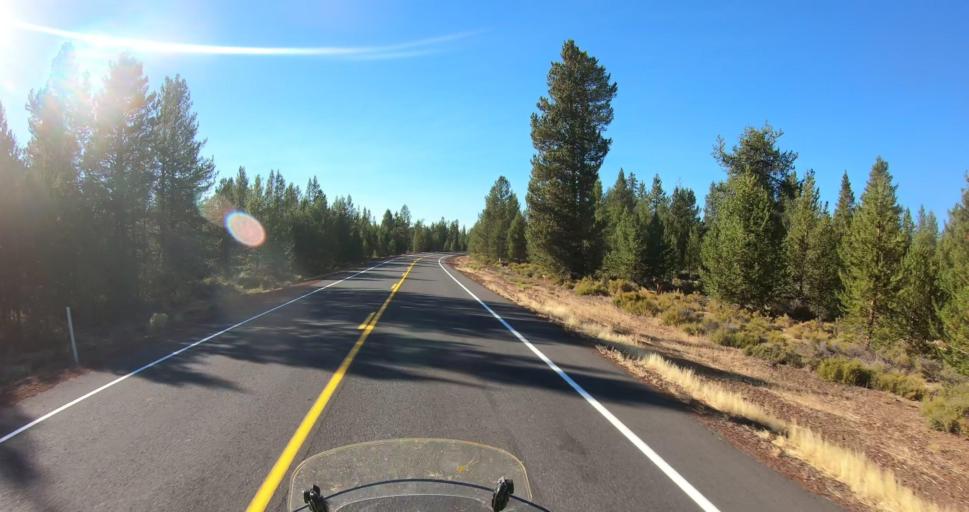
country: US
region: Oregon
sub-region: Deschutes County
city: La Pine
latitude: 43.4548
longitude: -121.3747
